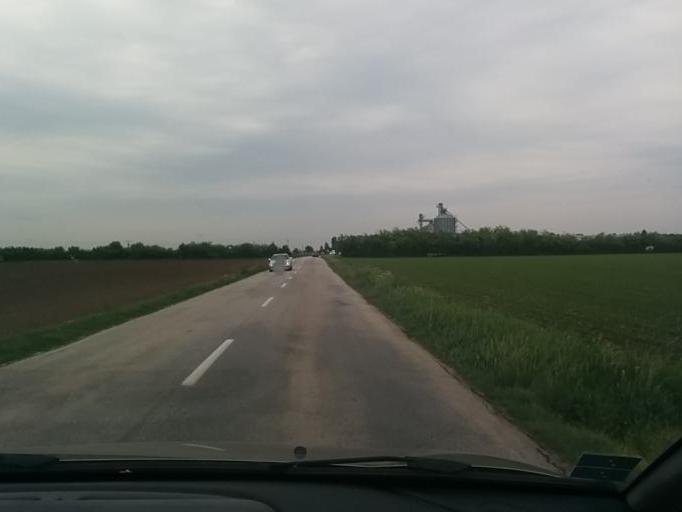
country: SK
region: Trnavsky
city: Sladkovicovo
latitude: 48.2188
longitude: 17.5931
